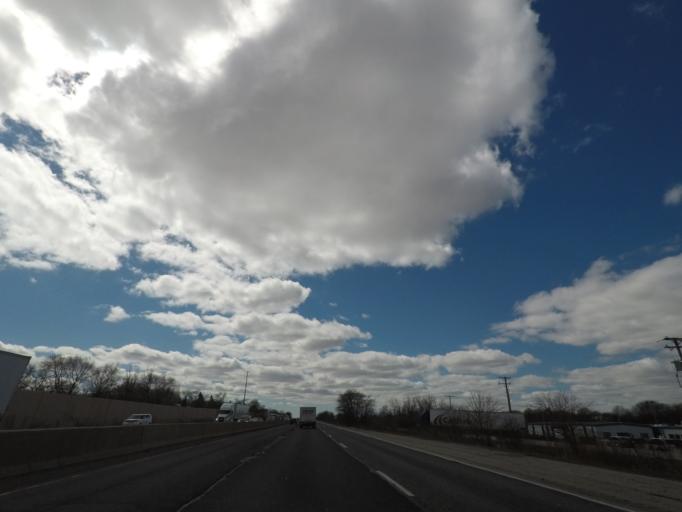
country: US
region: Illinois
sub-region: Will County
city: Crystal Lawns
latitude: 41.5545
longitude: -88.1806
